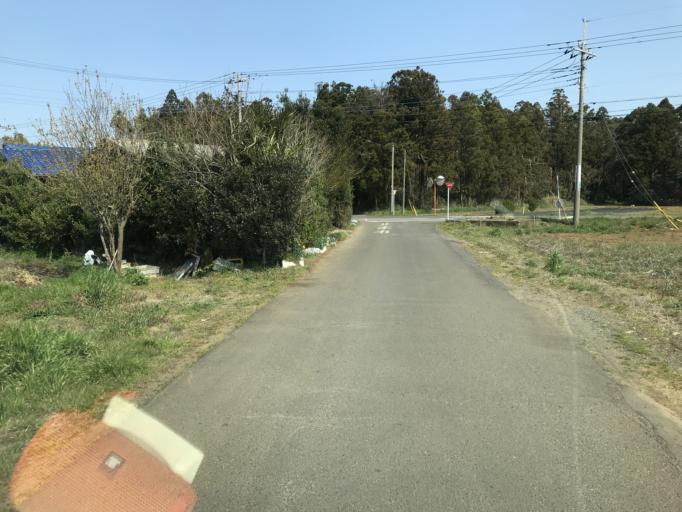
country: JP
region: Chiba
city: Sawara
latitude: 35.8424
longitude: 140.5249
